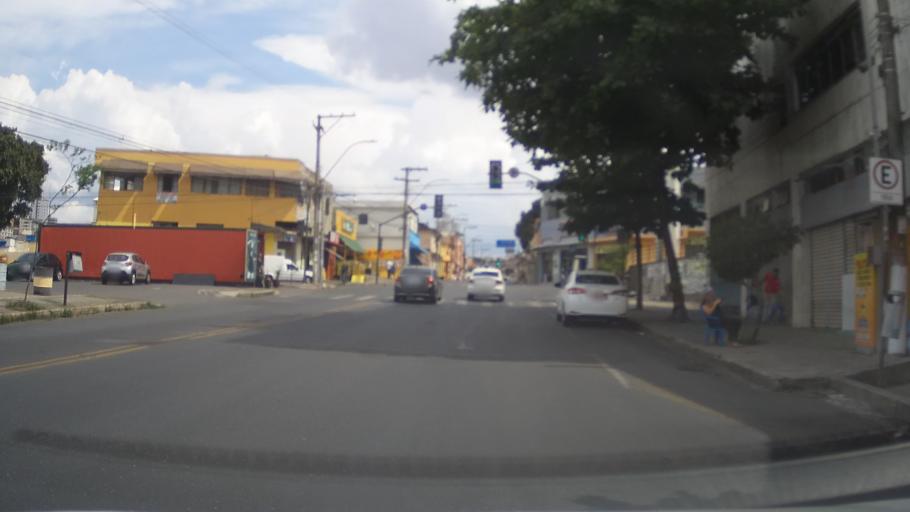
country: BR
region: Minas Gerais
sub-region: Belo Horizonte
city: Belo Horizonte
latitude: -19.8891
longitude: -43.9361
